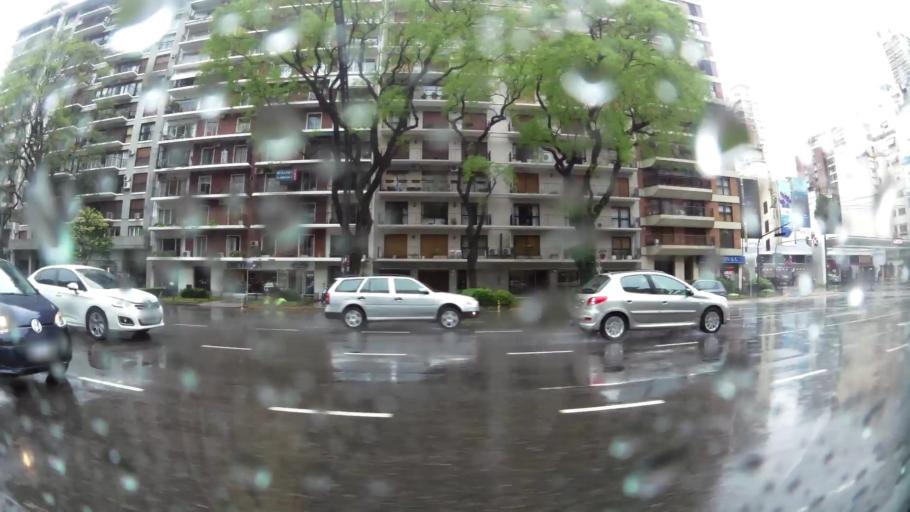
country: AR
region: Buenos Aires F.D.
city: Retiro
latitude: -34.5786
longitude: -58.4072
